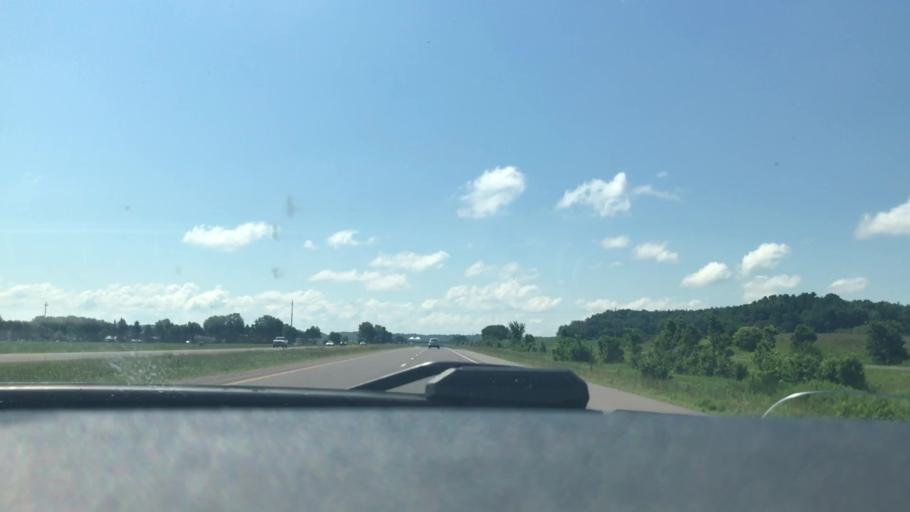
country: US
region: Wisconsin
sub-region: Chippewa County
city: Chippewa Falls
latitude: 45.0119
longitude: -91.4426
